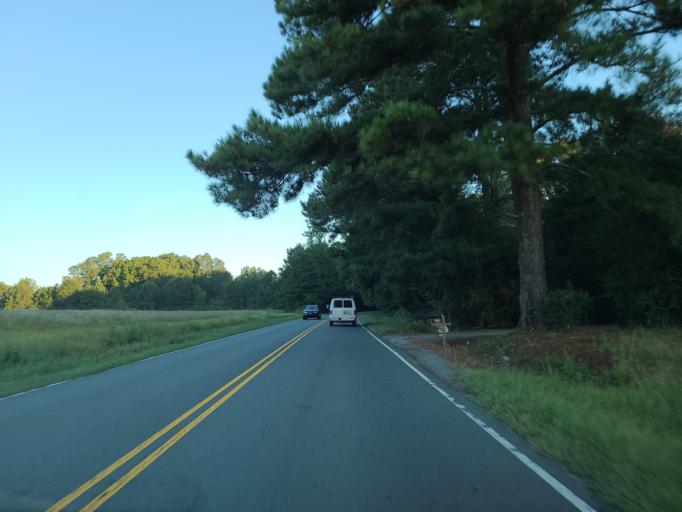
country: US
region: North Carolina
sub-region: Union County
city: Weddington
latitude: 35.0050
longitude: -80.7379
